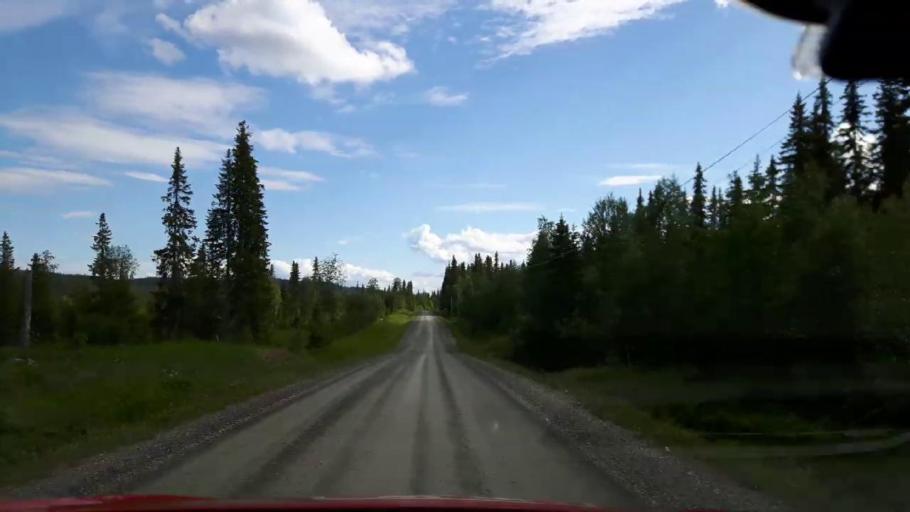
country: SE
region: Jaemtland
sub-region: Krokoms Kommun
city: Valla
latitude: 63.8118
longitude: 14.0493
